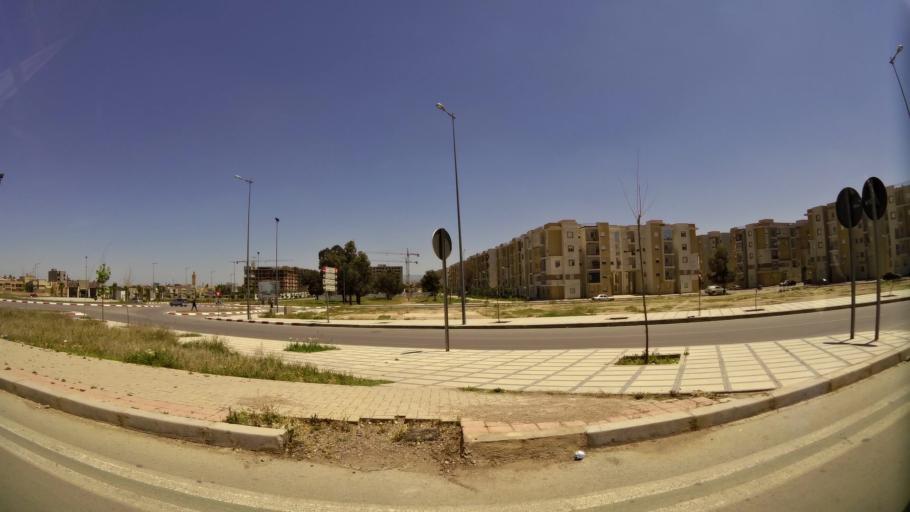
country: MA
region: Oriental
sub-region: Oujda-Angad
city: Oujda
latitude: 34.6645
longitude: -1.9186
